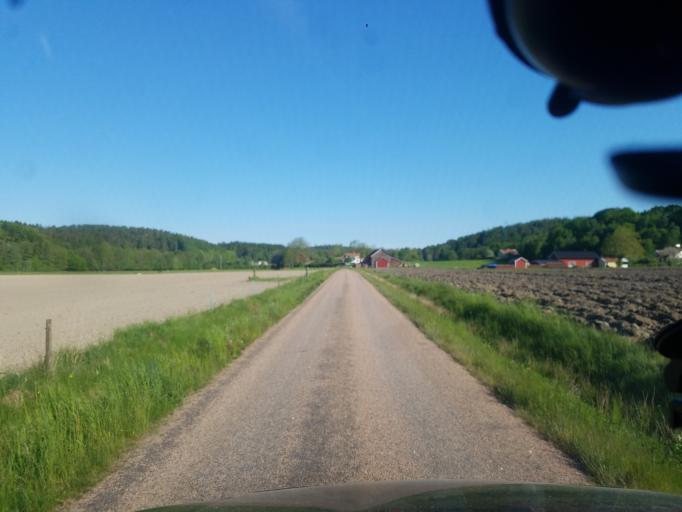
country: SE
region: Vaestra Goetaland
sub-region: Orust
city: Henan
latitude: 58.2878
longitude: 11.6393
